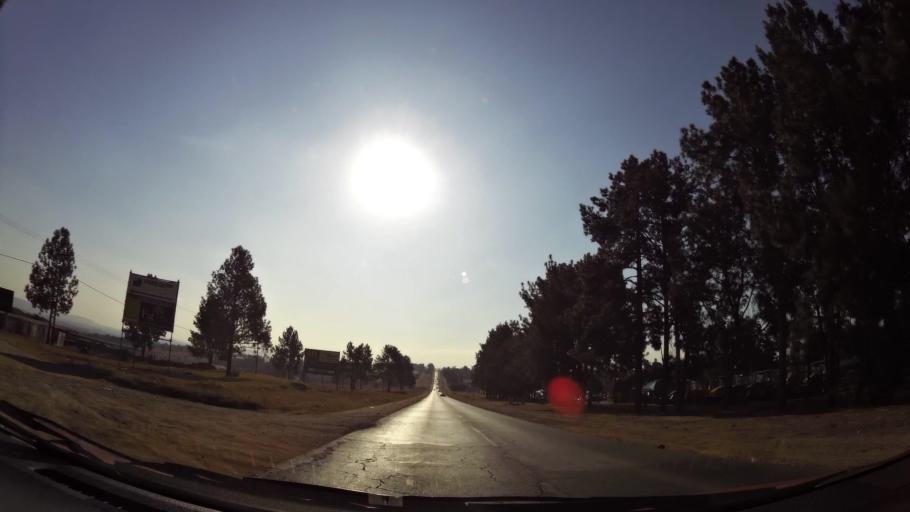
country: ZA
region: Gauteng
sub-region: West Rand District Municipality
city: Muldersdriseloop
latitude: -26.0497
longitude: 27.8916
